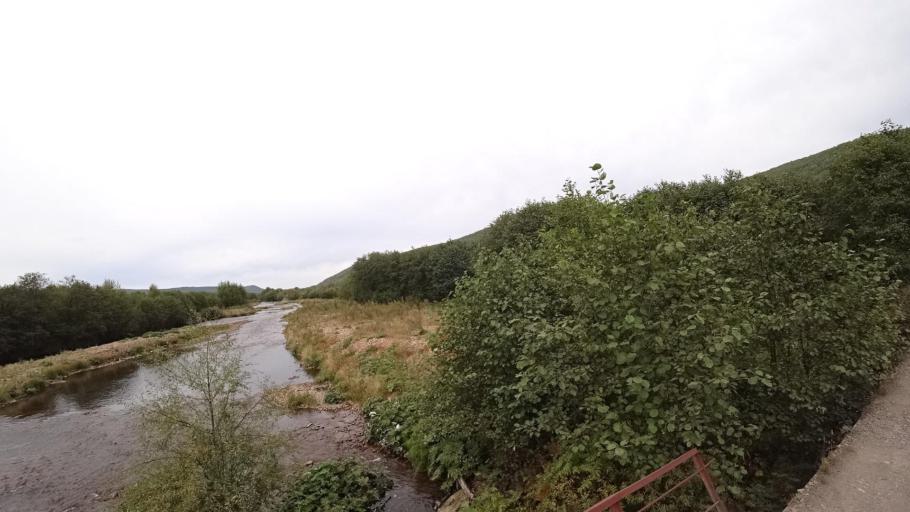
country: RU
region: Jewish Autonomous Oblast
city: Khingansk
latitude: 49.0337
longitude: 131.0527
